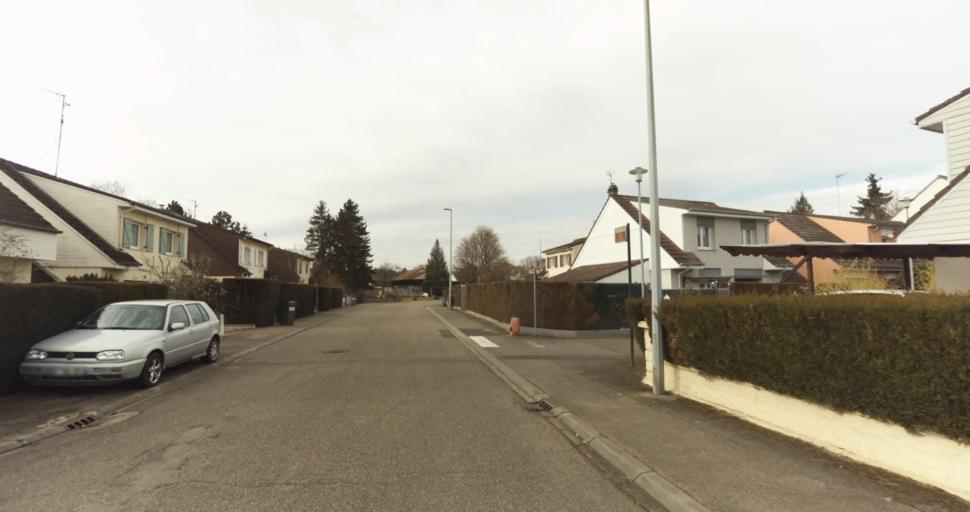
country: FR
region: Lorraine
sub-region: Departement de Meurthe-et-Moselle
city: Jarny
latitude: 49.1577
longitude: 5.8700
